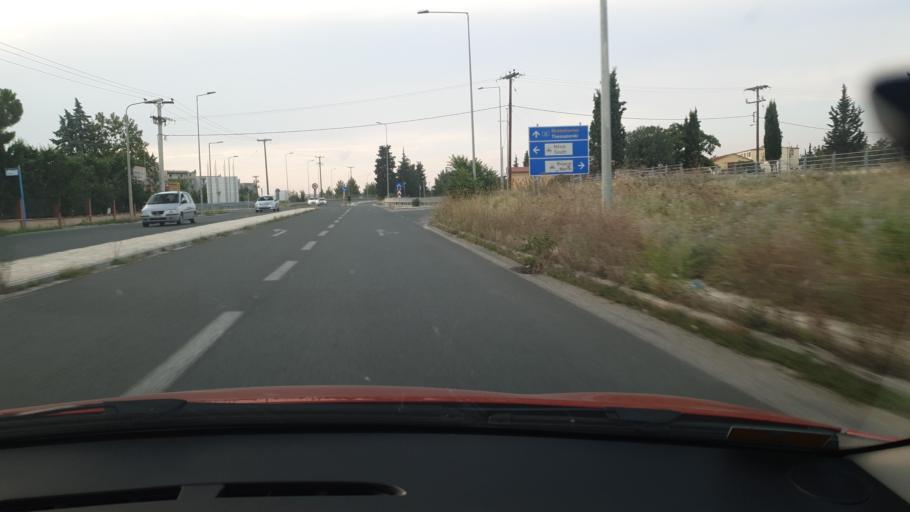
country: GR
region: Central Macedonia
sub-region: Nomos Thessalonikis
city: Thermi
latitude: 40.5324
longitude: 23.0398
